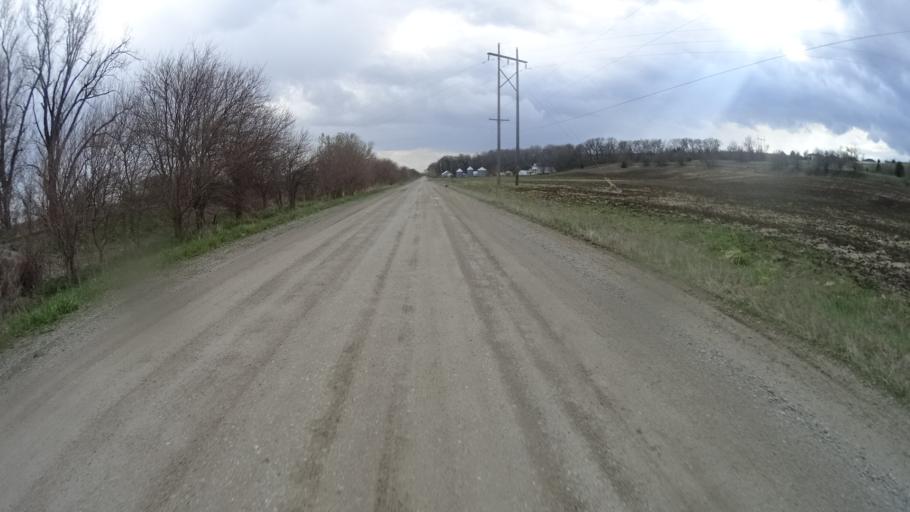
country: US
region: Nebraska
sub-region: Sarpy County
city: Offutt Air Force Base
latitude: 41.0909
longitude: -95.9145
